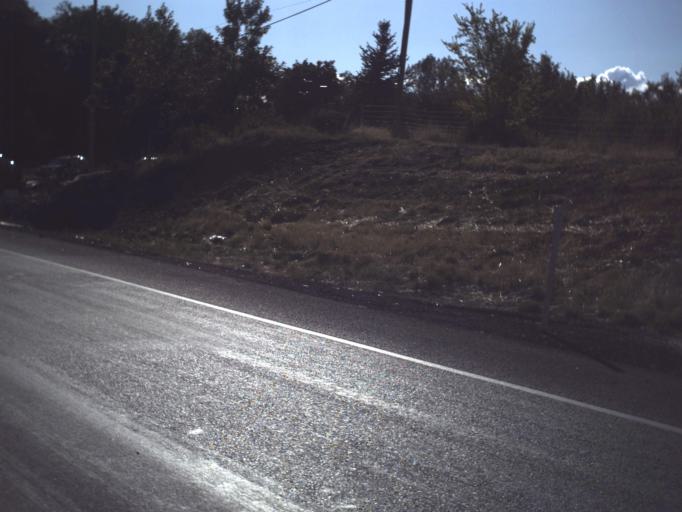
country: US
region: Utah
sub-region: Utah County
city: Santaquin
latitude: 39.9760
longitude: -111.7730
